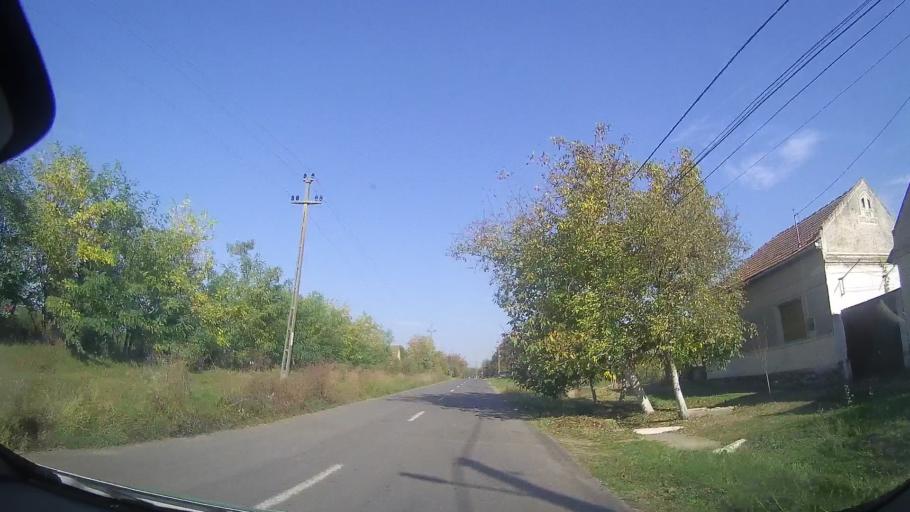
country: RO
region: Timis
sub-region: Comuna Topolovatu Mare
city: Topolovatu Mare
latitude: 45.8161
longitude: 21.5805
